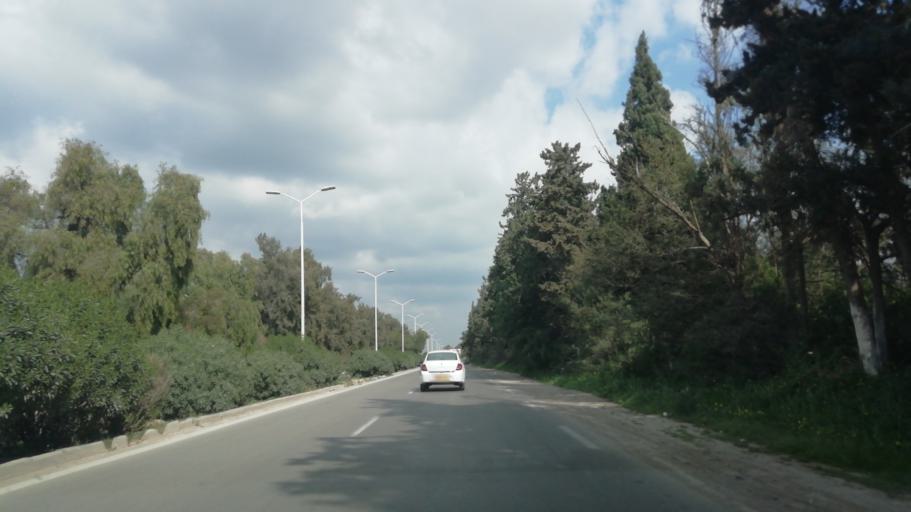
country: DZ
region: Mascara
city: Mascara
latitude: 35.6022
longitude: 0.0858
